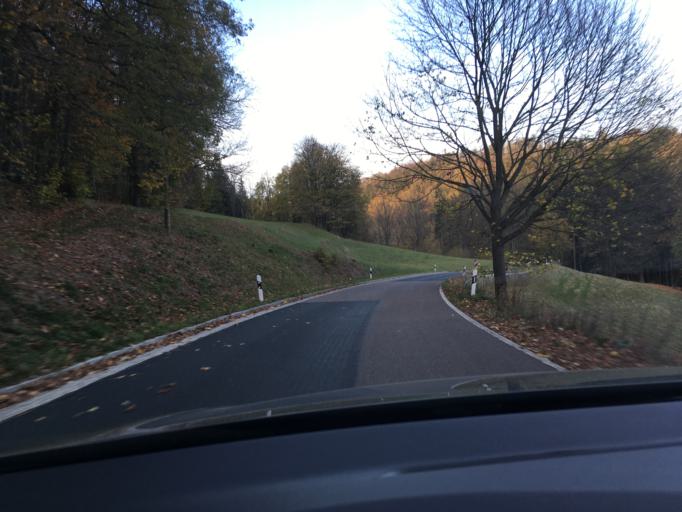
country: DE
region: Saxony
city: Barenstein
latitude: 50.8175
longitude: 13.8232
